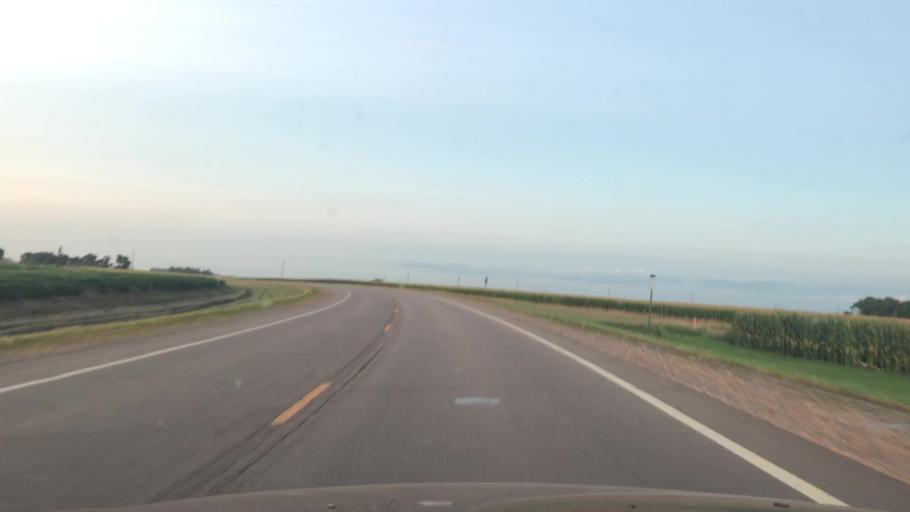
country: US
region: Minnesota
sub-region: Redwood County
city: Redwood Falls
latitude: 44.4196
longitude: -95.1186
